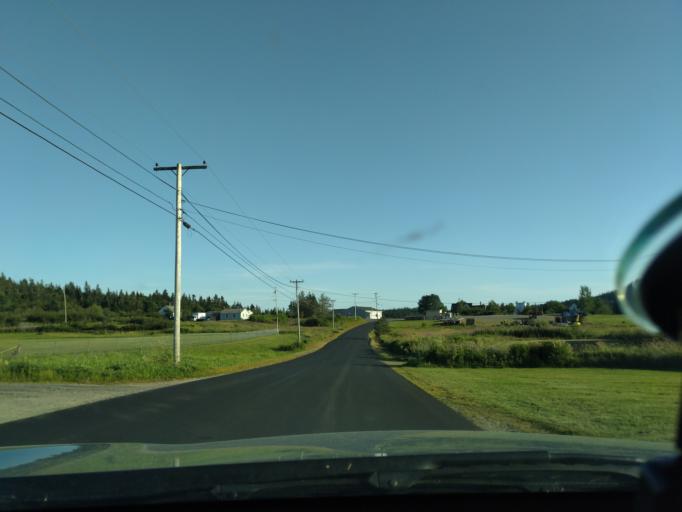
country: US
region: Maine
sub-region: Washington County
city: Machiasport
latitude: 44.6605
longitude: -67.2031
